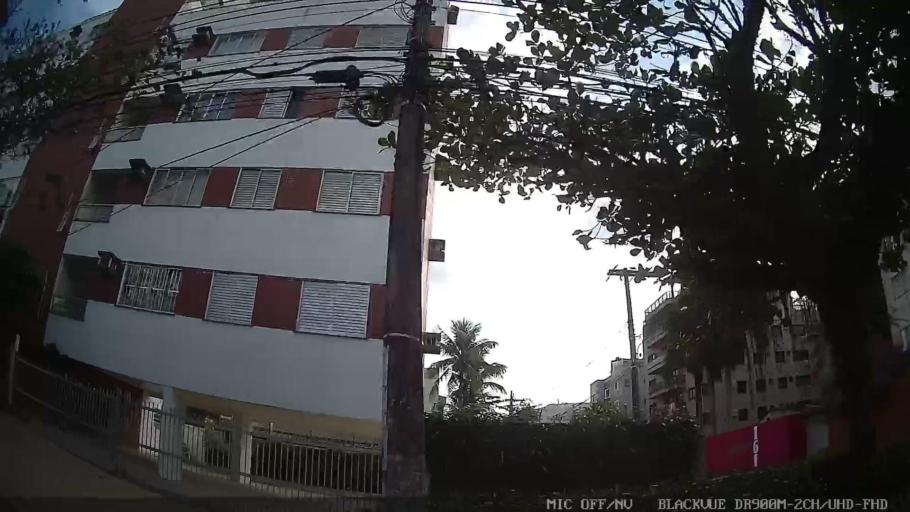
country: BR
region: Sao Paulo
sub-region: Guaruja
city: Guaruja
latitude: -23.9822
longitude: -46.2358
